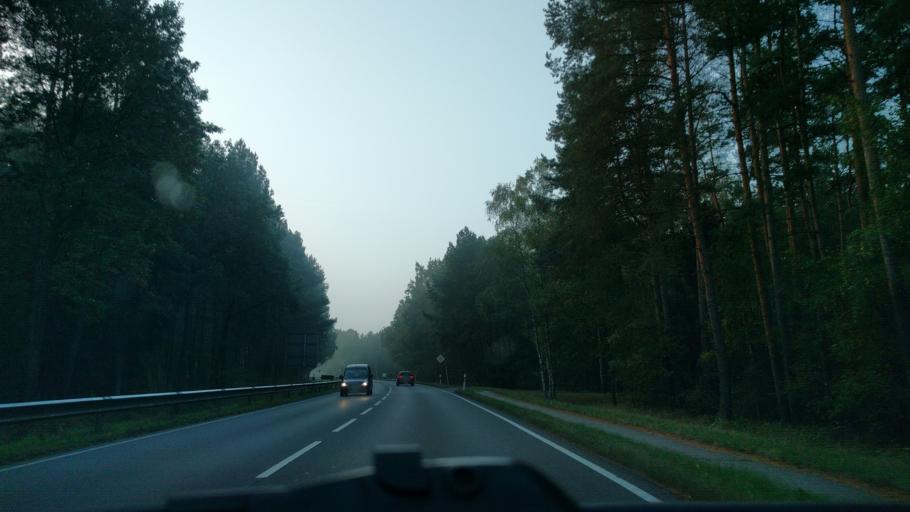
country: DE
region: Lower Saxony
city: Isenbuttel
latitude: 52.4588
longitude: 10.5777
